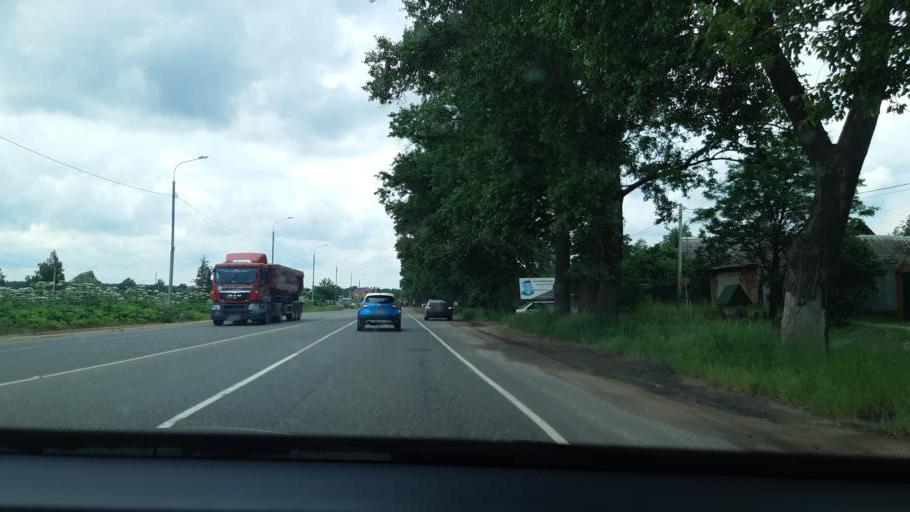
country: RU
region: Moskovskaya
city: Chupryakovo
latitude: 55.5588
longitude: 36.5682
